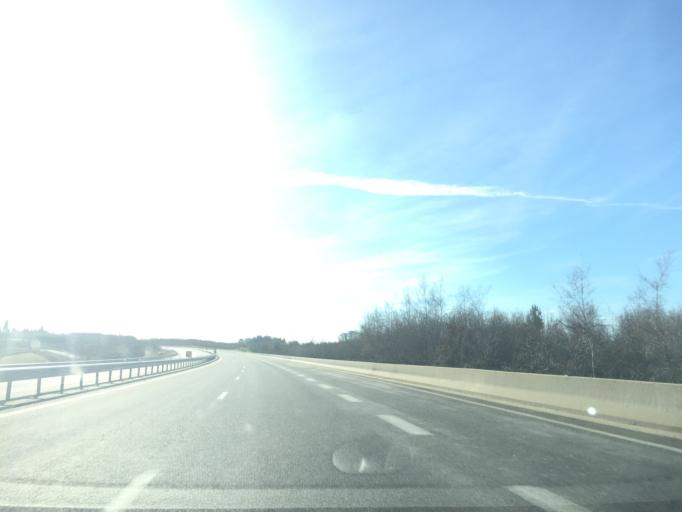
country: FR
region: Auvergne
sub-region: Departement du Puy-de-Dome
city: Gelles
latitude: 45.7243
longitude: 2.6942
